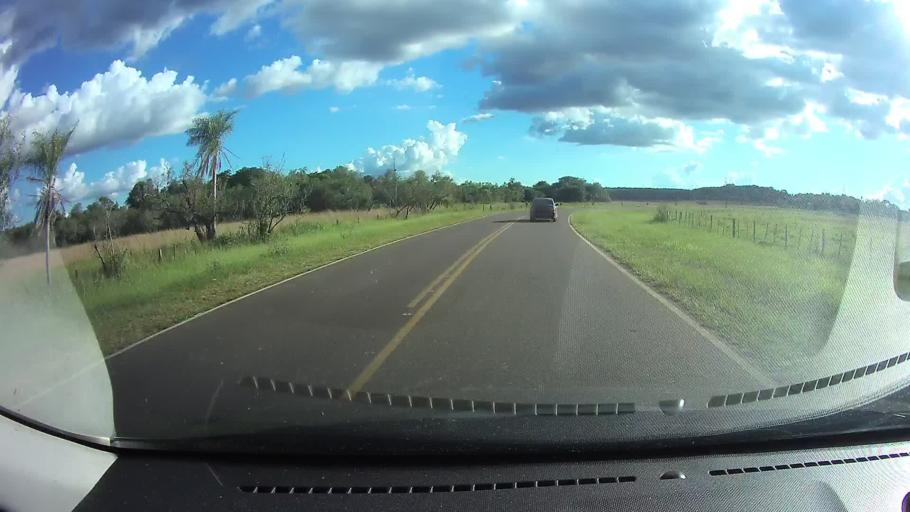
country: PY
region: Cordillera
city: Atyra
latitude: -25.2833
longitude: -57.1859
